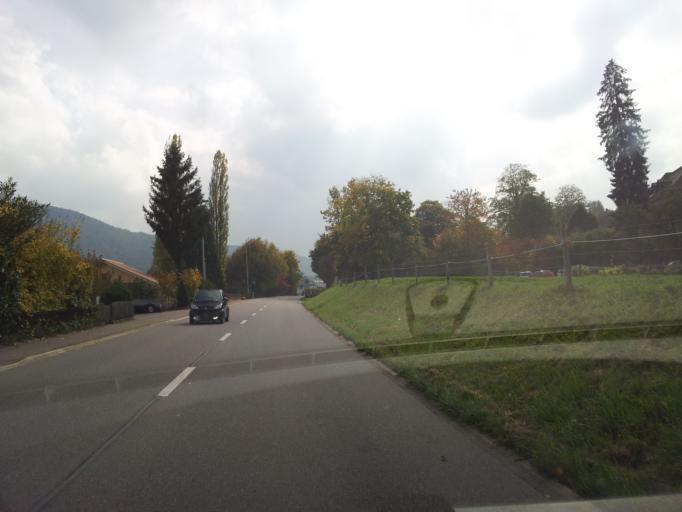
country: CH
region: Bern
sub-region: Bern-Mittelland District
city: Belp
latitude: 46.8904
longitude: 7.4949
